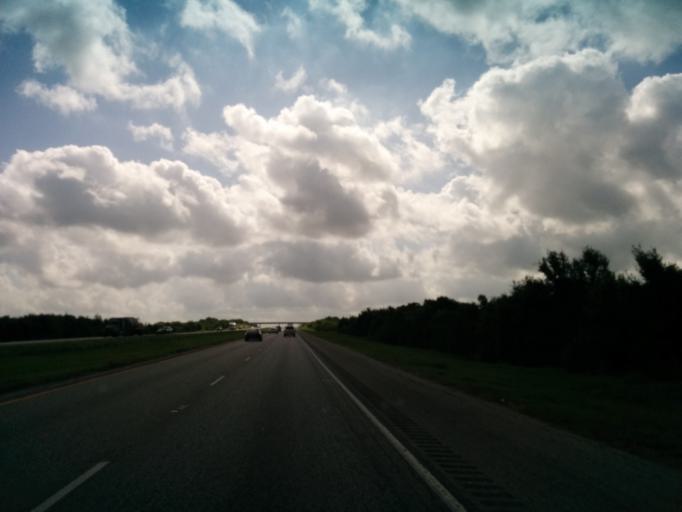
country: US
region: Texas
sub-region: Gonzales County
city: Waelder
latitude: 29.6658
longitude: -97.3427
